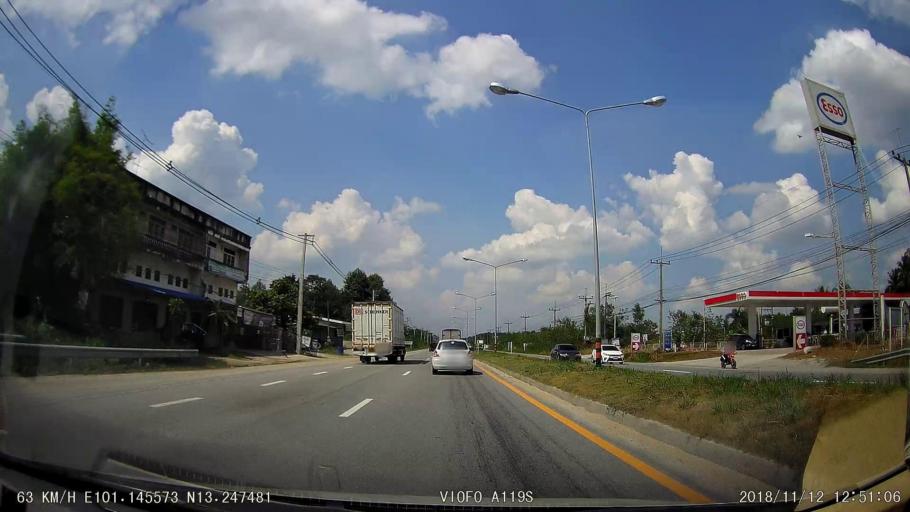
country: TH
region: Chon Buri
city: Ban Bueng
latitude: 13.2477
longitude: 101.1455
